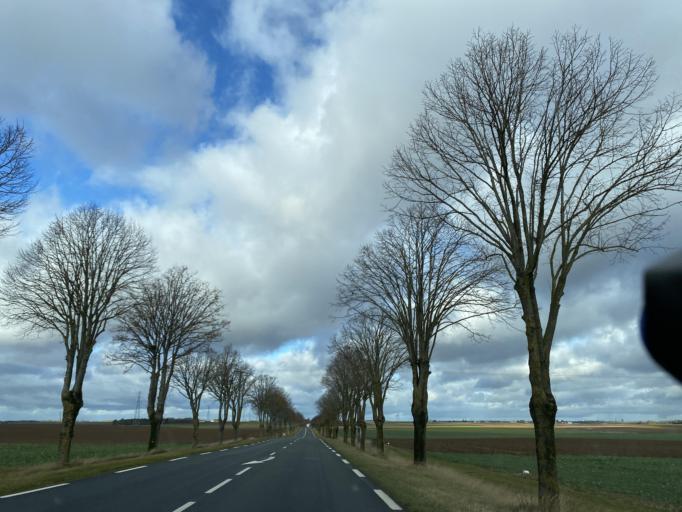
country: FR
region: Centre
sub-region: Departement d'Eure-et-Loir
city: Baigneaux
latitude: 48.1535
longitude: 1.8436
